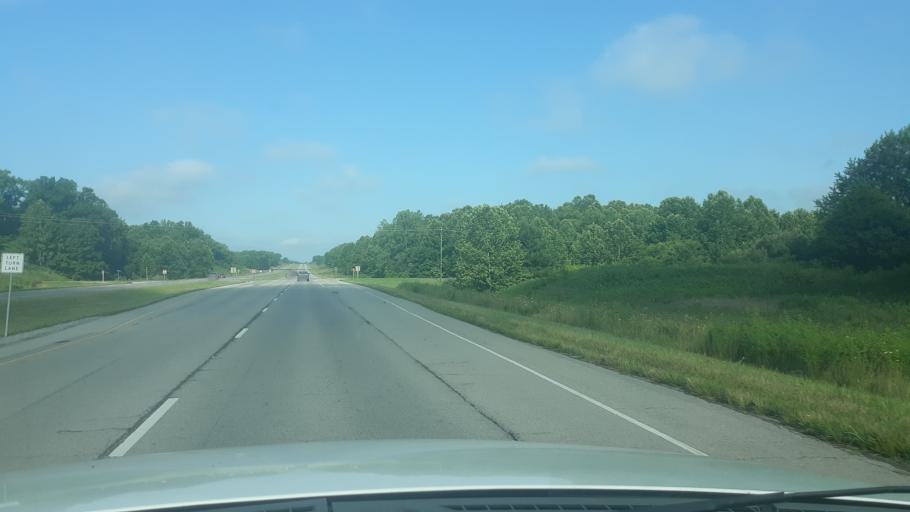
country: US
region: Illinois
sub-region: Saline County
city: Carrier Mills
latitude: 37.7307
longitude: -88.7503
